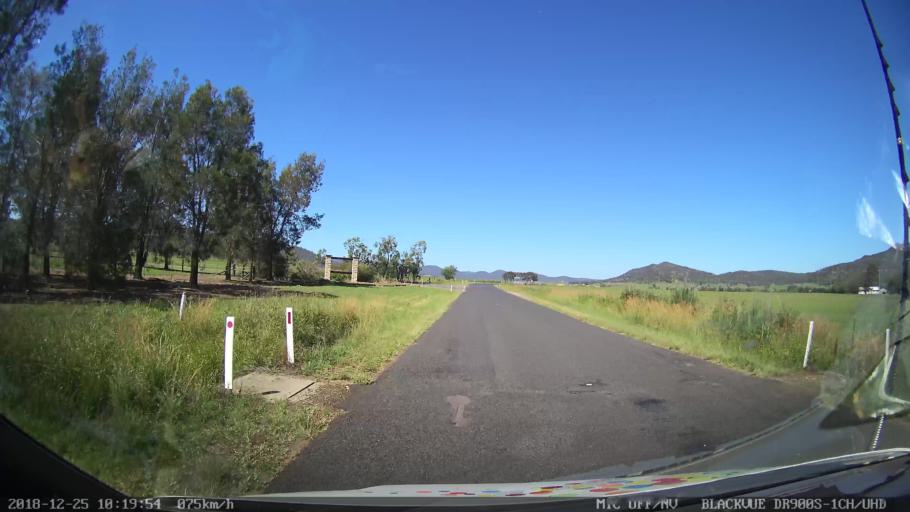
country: AU
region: New South Wales
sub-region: Muswellbrook
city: Denman
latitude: -32.3549
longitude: 150.5546
